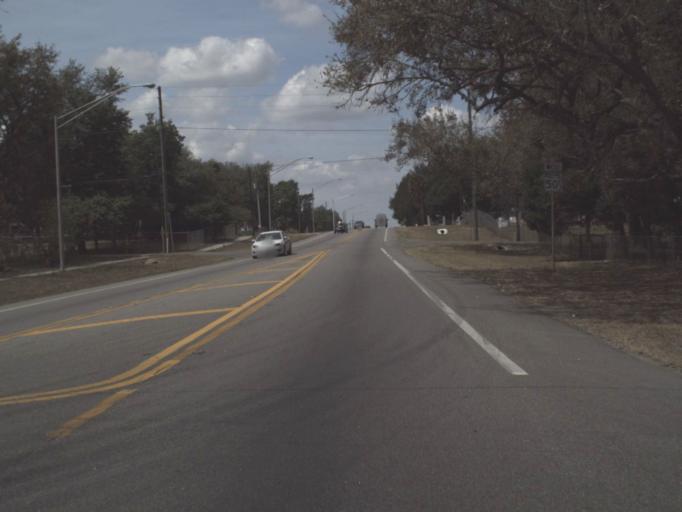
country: US
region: Florida
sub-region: Lake County
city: Mascotte
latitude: 28.5785
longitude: -81.8950
